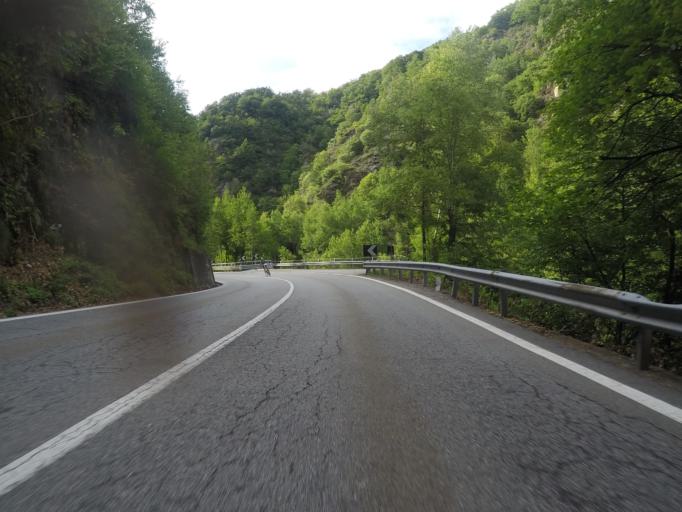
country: IT
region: Piedmont
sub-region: Provincia Verbano-Cusio-Ossola
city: Trontano
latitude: 46.1254
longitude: 8.3474
